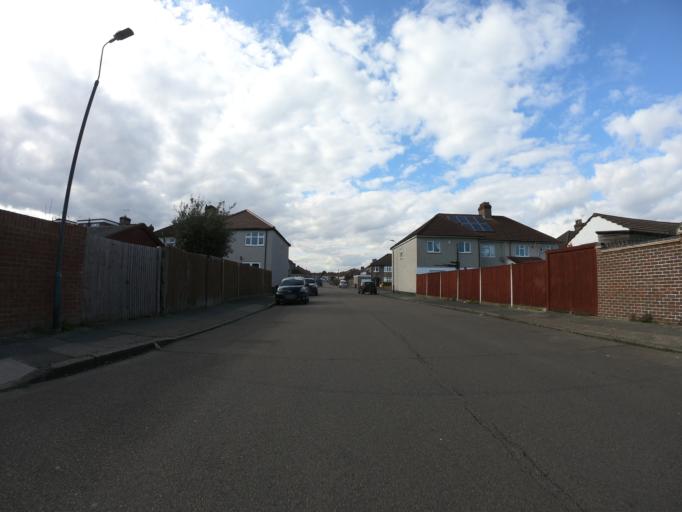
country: GB
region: England
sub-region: Greater London
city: Bexleyheath
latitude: 51.4744
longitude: 0.1377
